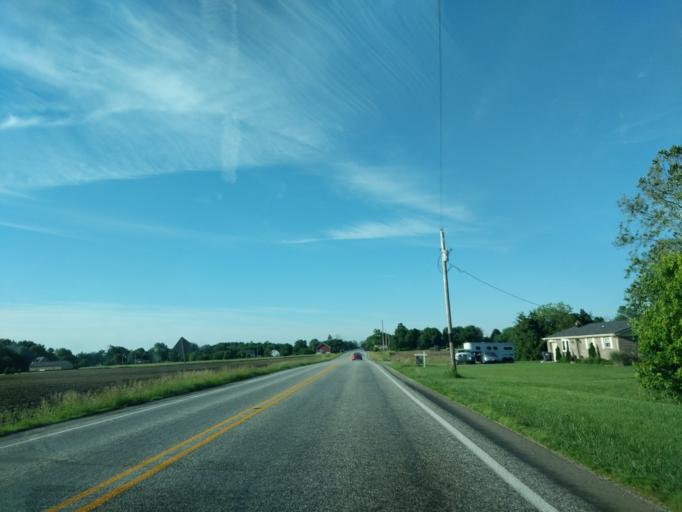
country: US
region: Indiana
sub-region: Madison County
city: Ingalls
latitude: 39.9347
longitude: -85.7712
